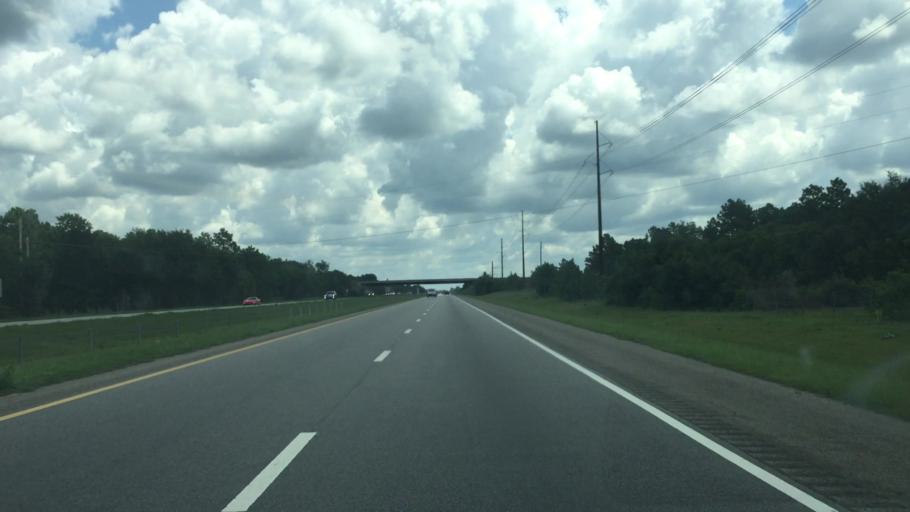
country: US
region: North Carolina
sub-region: Richmond County
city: Hamlet
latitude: 34.8590
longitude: -79.6807
